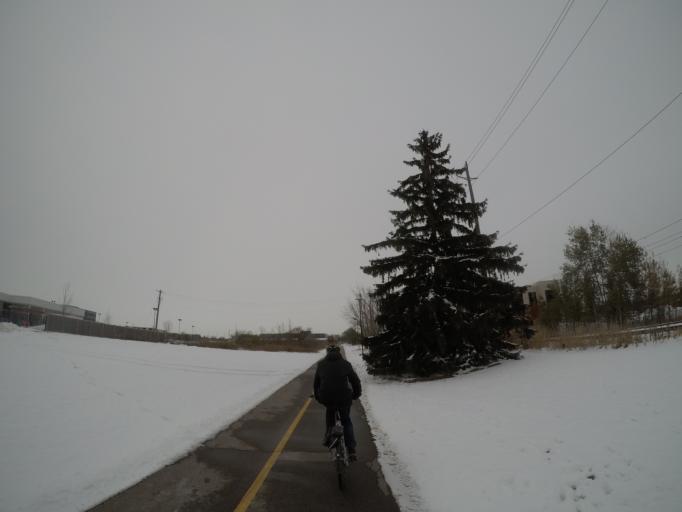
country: CA
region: Ontario
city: Waterloo
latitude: 43.4770
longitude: -80.5438
